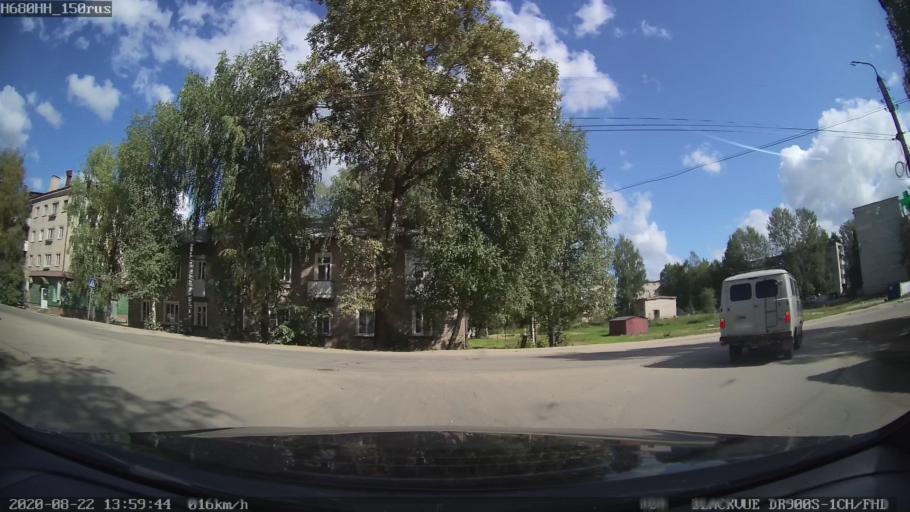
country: RU
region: Tverskaya
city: Bezhetsk
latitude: 57.7857
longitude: 36.6995
